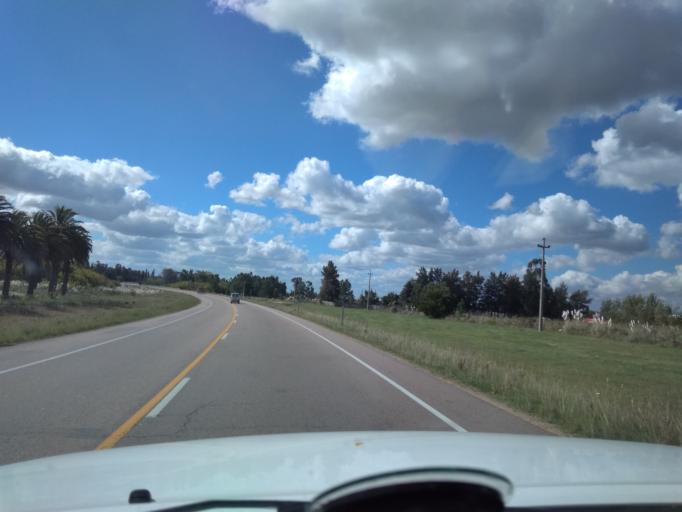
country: UY
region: Canelones
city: Sauce
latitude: -34.6769
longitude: -56.0513
